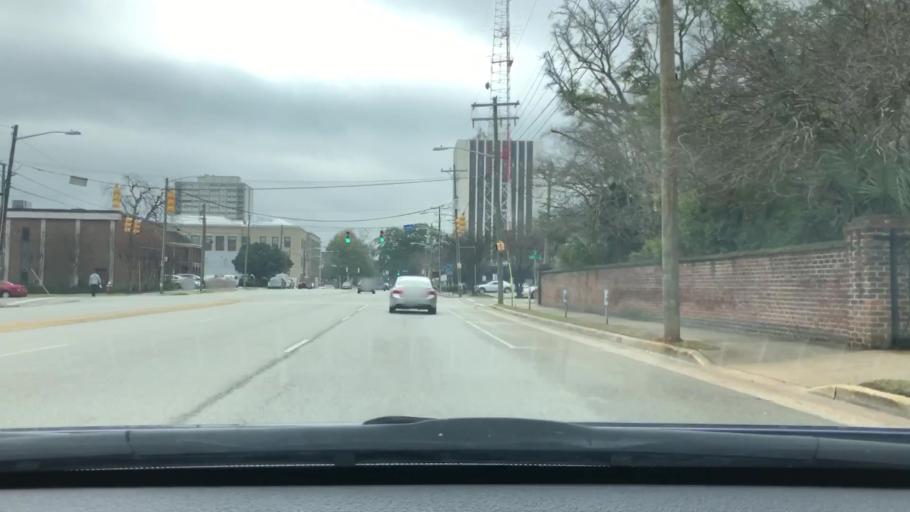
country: US
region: South Carolina
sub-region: Richland County
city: Columbia
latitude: 34.0045
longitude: -81.0296
